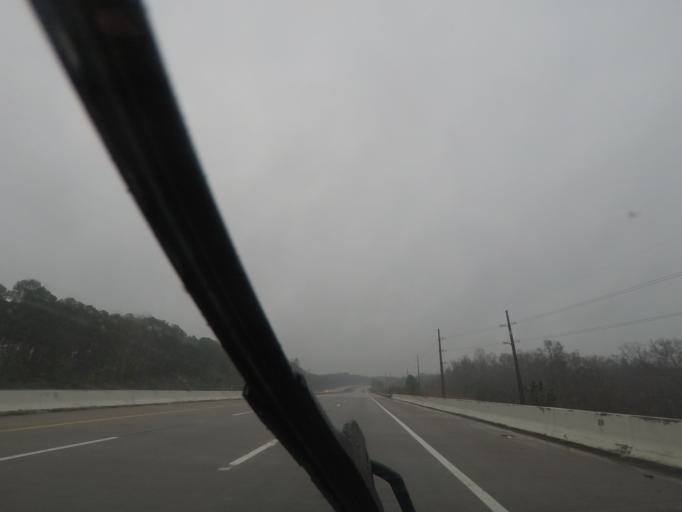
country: US
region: North Carolina
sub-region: Wake County
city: Green Level
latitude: 35.7773
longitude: -78.8858
